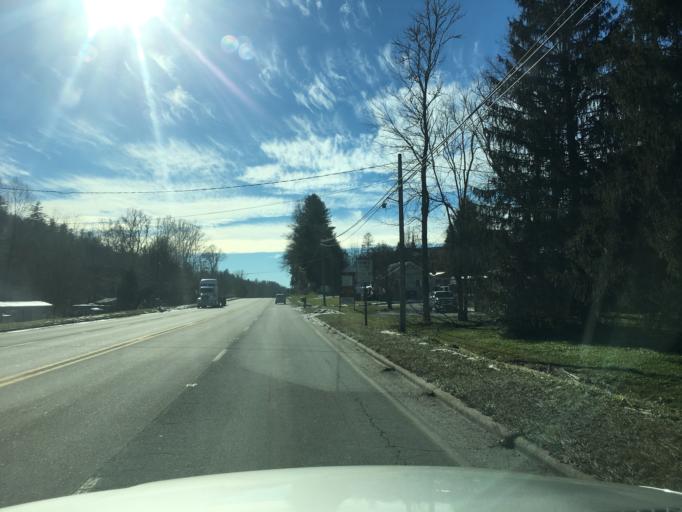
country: US
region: North Carolina
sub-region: Transylvania County
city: Brevard
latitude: 35.2869
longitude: -82.6893
